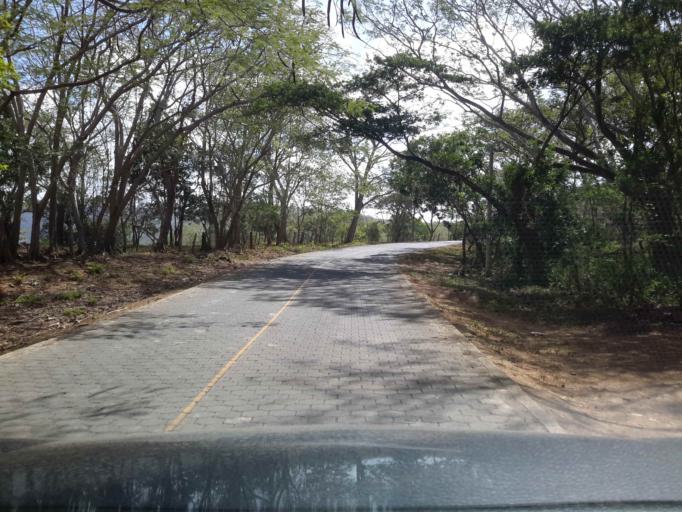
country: NI
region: Rivas
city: San Juan del Sur
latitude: 11.2439
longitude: -85.8366
